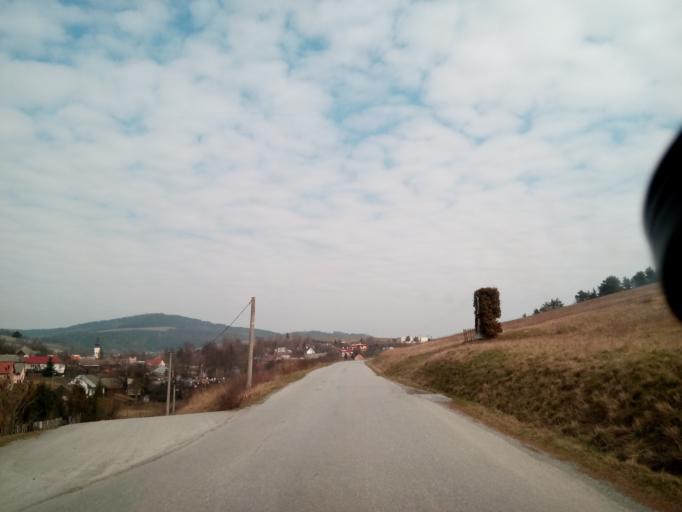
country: SK
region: Presovsky
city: Sabinov
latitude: 49.0390
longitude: 21.0182
